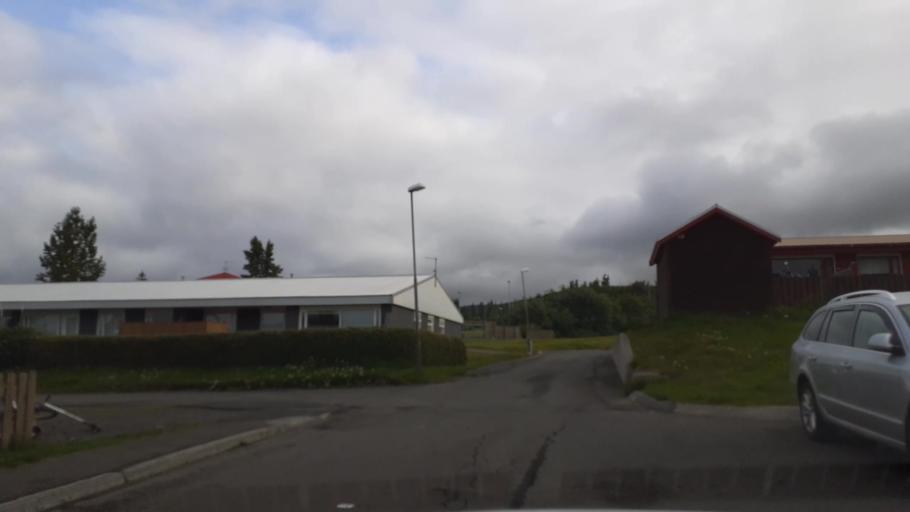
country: IS
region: Northeast
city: Akureyri
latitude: 65.7476
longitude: -18.0819
